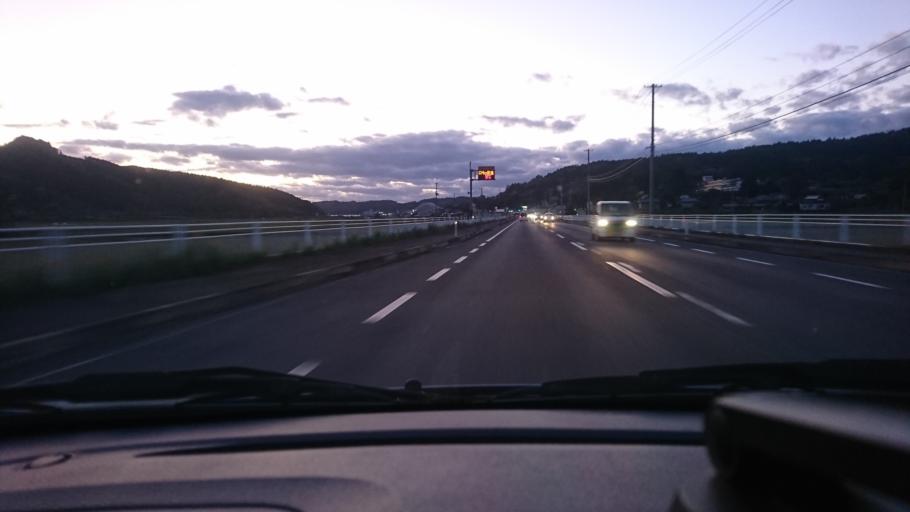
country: JP
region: Iwate
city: Ichinoseki
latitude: 38.8997
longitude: 141.2898
